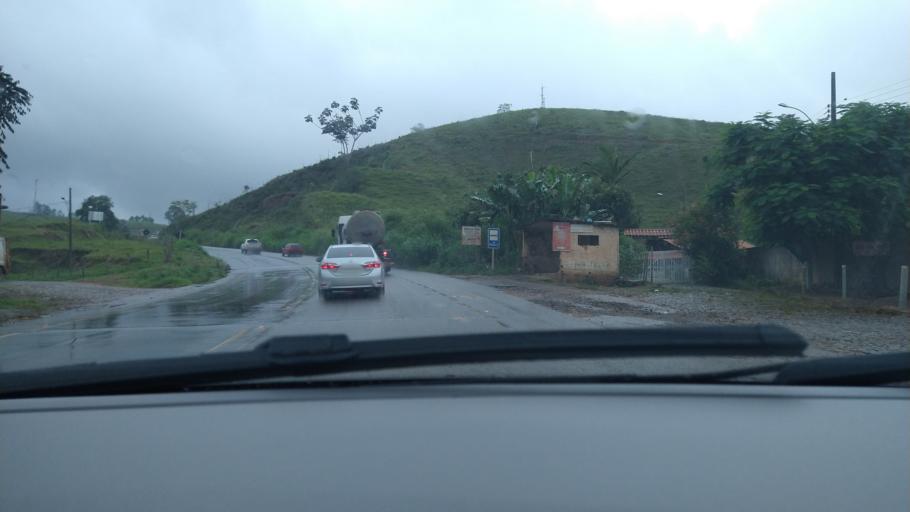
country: BR
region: Minas Gerais
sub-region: Vicosa
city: Vicosa
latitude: -20.5985
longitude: -42.8746
